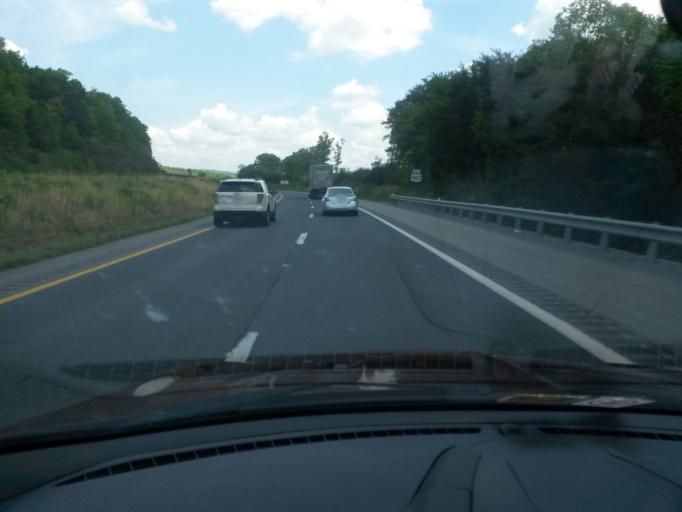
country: US
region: Virginia
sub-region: Campbell County
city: Timberlake
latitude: 37.3129
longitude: -79.2300
